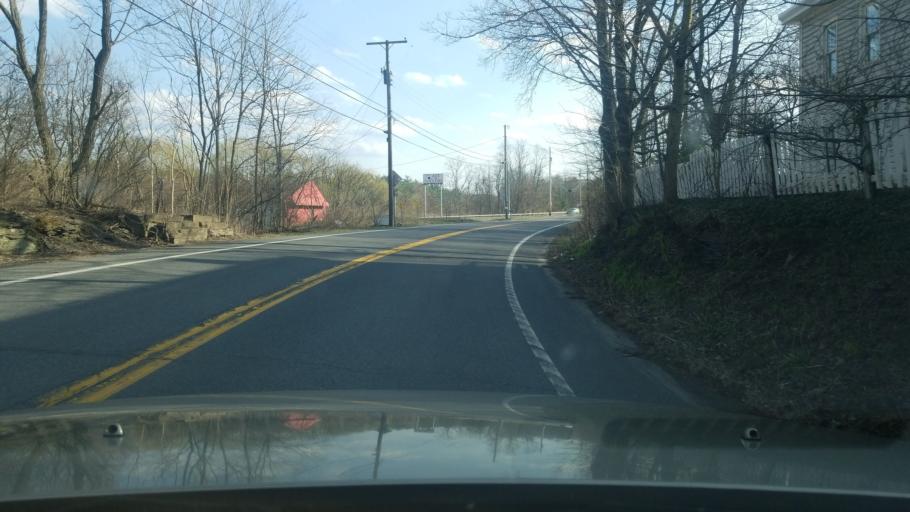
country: US
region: New York
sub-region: Greene County
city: Palenville
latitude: 42.1579
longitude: -73.9975
